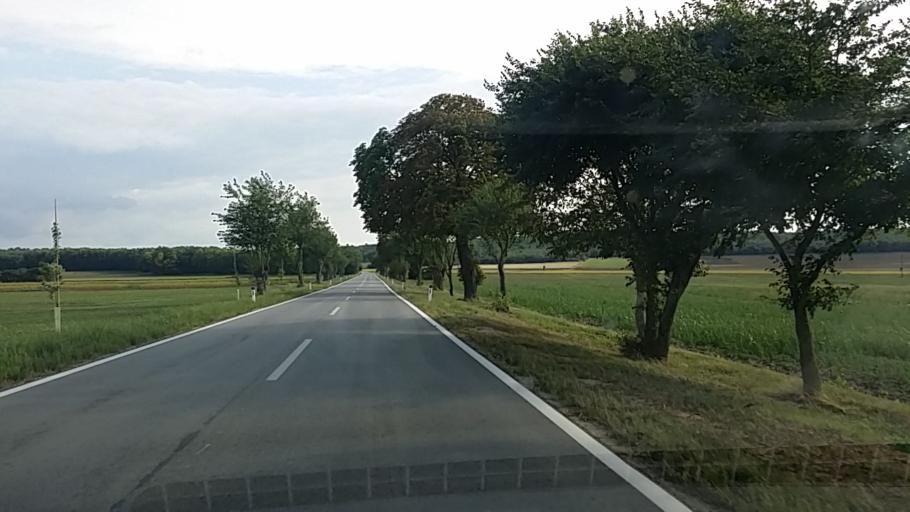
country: AT
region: Burgenland
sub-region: Eisenstadt-Umgebung
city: Sankt Margarethen im Burgenland
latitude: 47.7782
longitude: 16.6163
